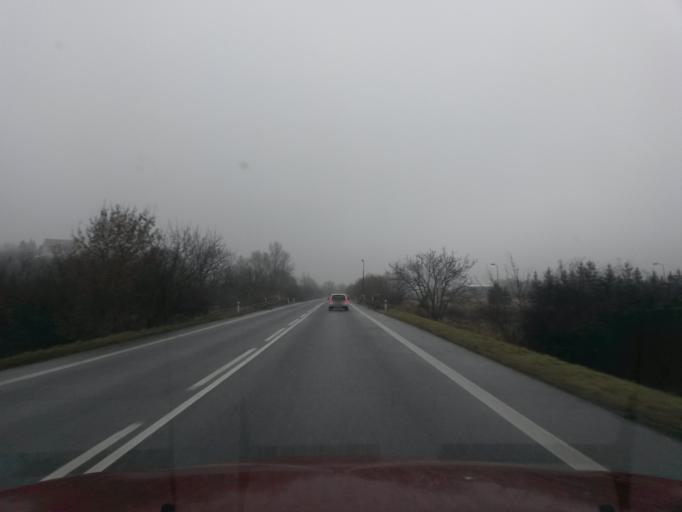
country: SK
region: Presovsky
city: Vranov nad Topl'ou
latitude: 48.8732
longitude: 21.6995
